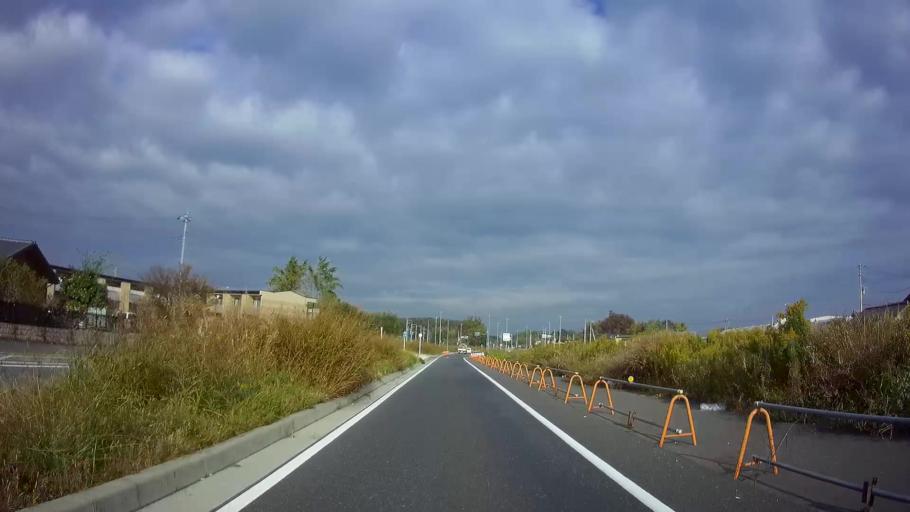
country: JP
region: Saitama
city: Okegawa
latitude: 35.9708
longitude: 139.5449
